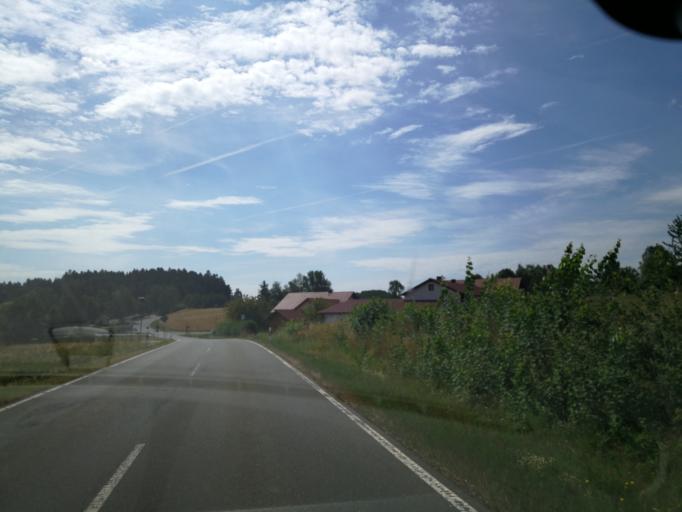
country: DE
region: Bavaria
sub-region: Upper Palatinate
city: Falkenstein
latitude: 49.0830
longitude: 12.5062
